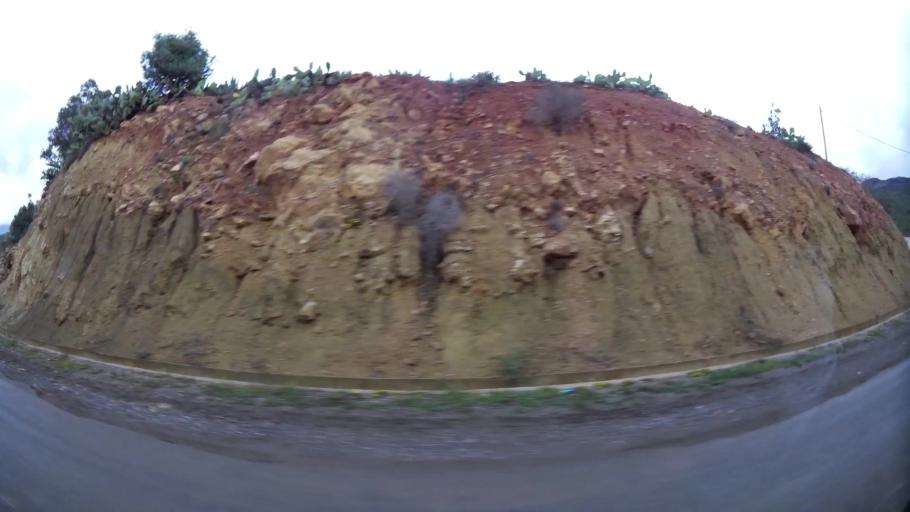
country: MA
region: Taza-Al Hoceima-Taounate
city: Imzourene
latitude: 34.9499
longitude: -3.8088
